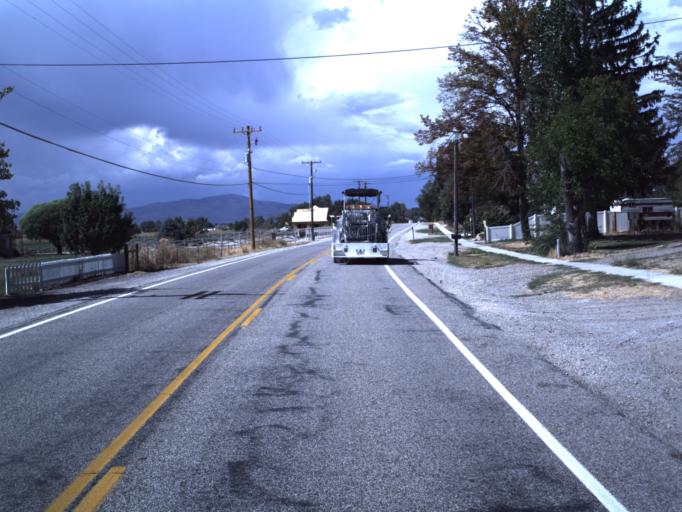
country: US
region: Utah
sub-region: Box Elder County
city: Honeyville
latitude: 41.6246
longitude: -112.0736
